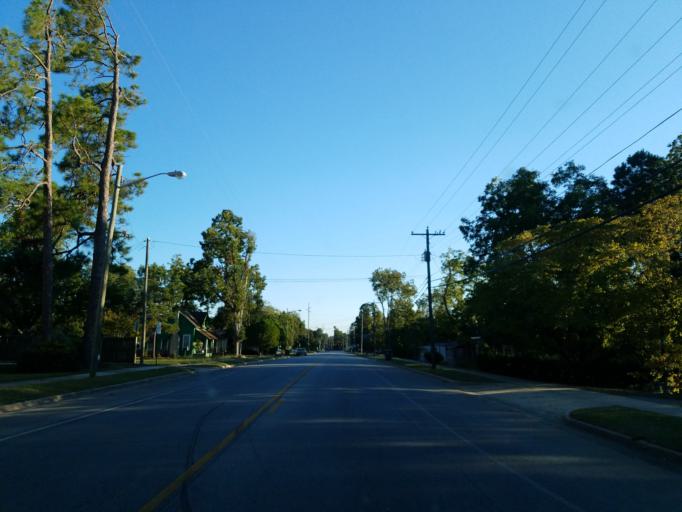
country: US
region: Georgia
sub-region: Worth County
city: Sylvester
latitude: 31.5353
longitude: -83.8440
